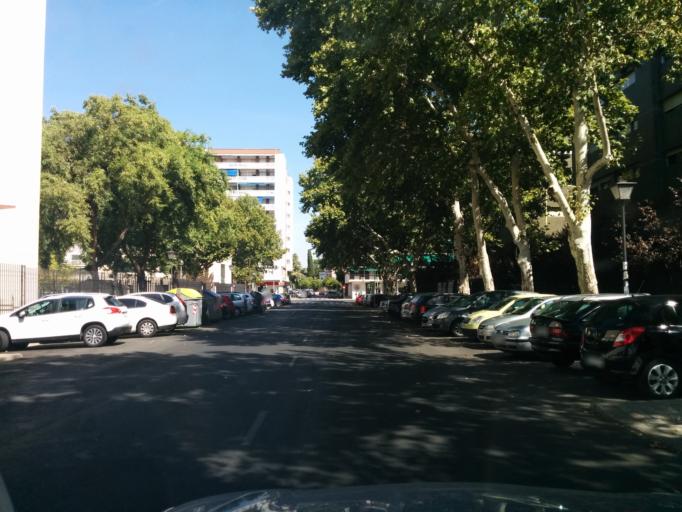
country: ES
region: Andalusia
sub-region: Provincia de Sevilla
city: Sevilla
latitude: 37.3608
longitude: -5.9875
